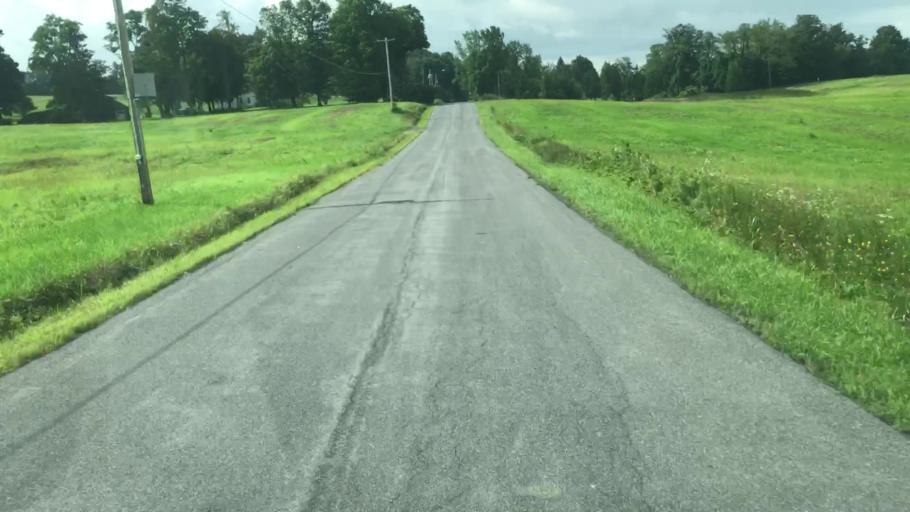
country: US
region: New York
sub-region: Onondaga County
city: Camillus
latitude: 43.0668
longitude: -76.3490
